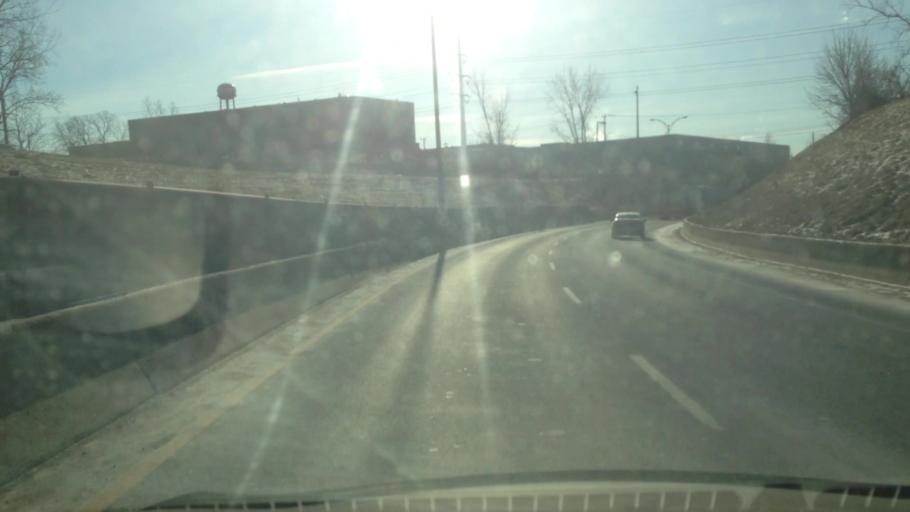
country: CA
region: Quebec
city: Montreal-Ouest
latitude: 45.4303
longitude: -73.6495
